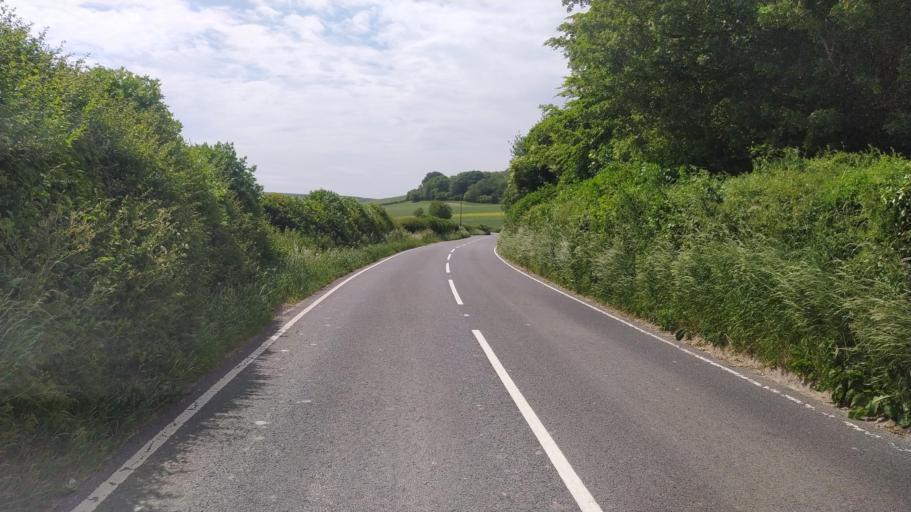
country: GB
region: England
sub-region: Dorset
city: Dorchester
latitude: 50.7943
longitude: -2.4787
